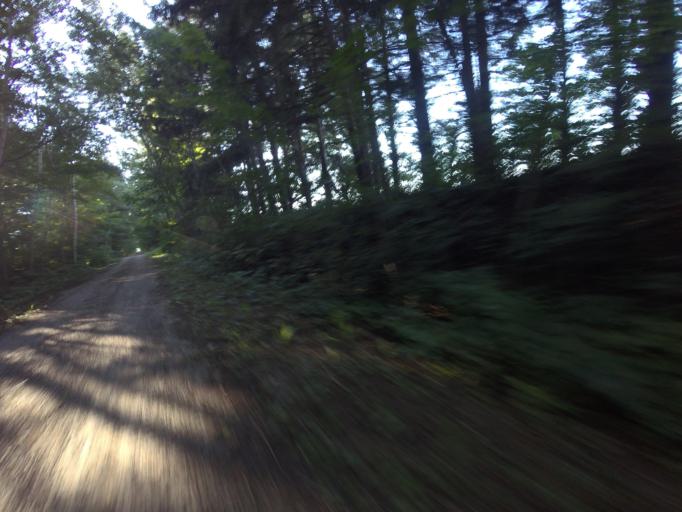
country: CA
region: Ontario
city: Goderich
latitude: 43.7528
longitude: -81.6669
